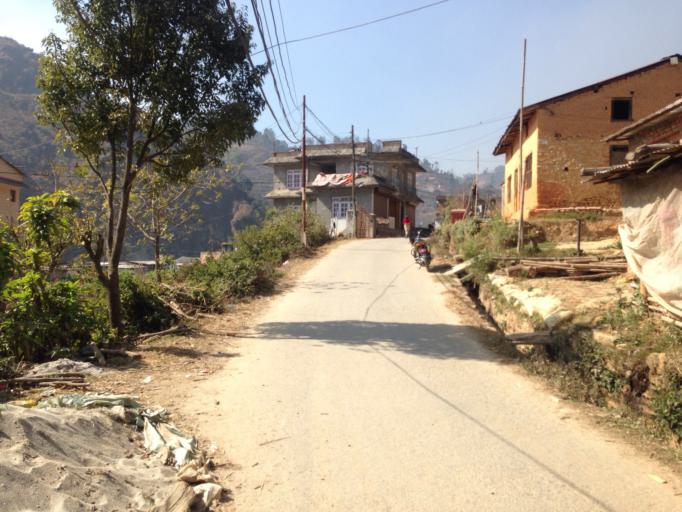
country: NP
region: Central Region
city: Kirtipur
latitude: 27.7258
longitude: 85.2706
